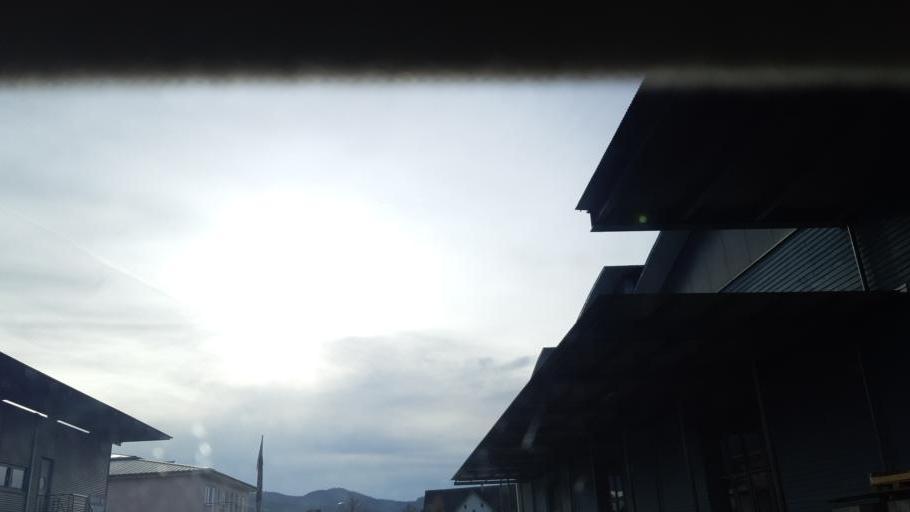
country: DE
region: Baden-Wuerttemberg
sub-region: Freiburg Region
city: Gutach im Breisgau
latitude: 48.1254
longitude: 7.9974
